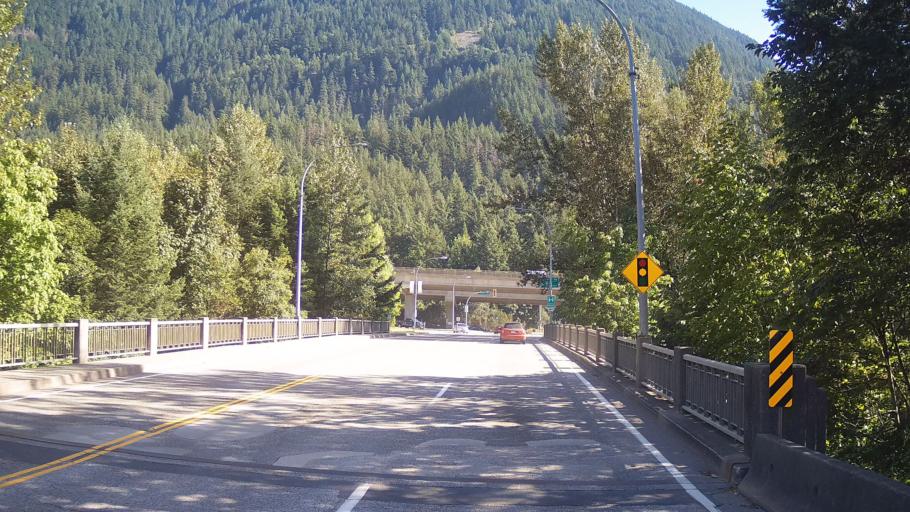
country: CA
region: British Columbia
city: Hope
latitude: 49.3748
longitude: -121.4419
